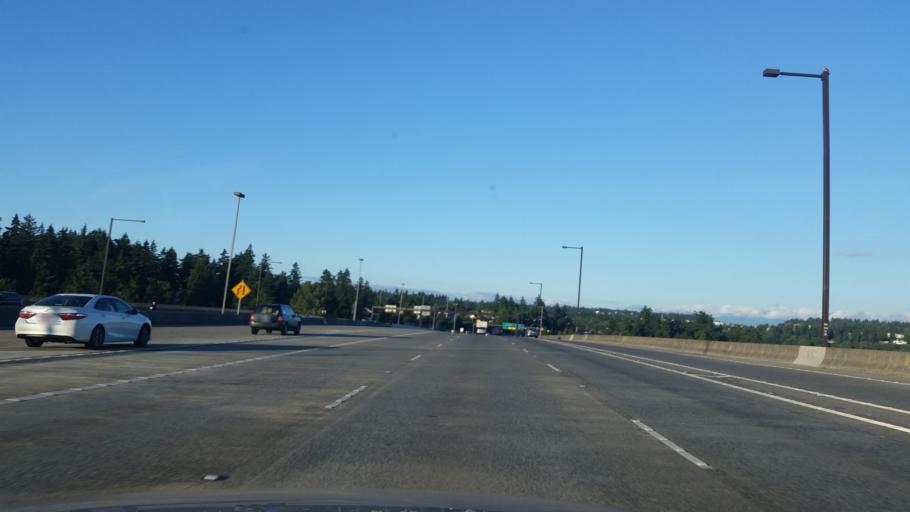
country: US
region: Washington
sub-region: King County
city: Newport
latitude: 47.5784
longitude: -122.2014
